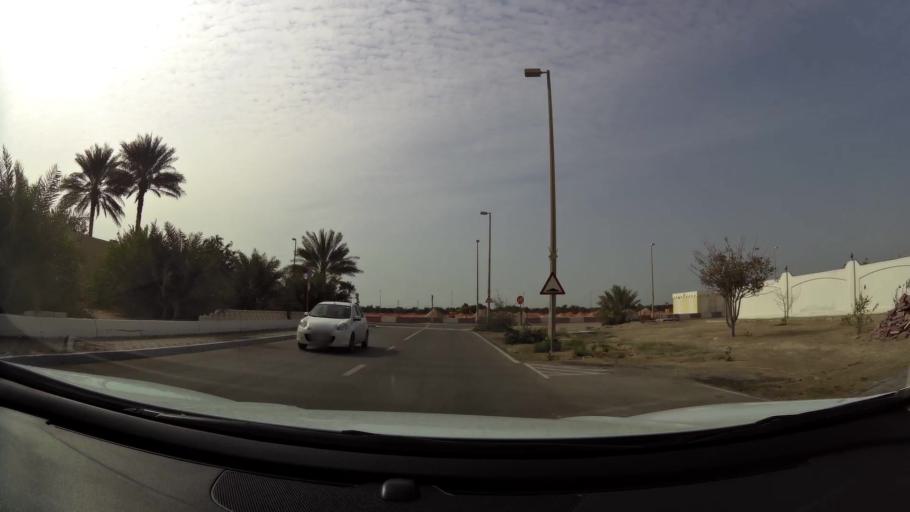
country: AE
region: Abu Dhabi
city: Abu Dhabi
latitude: 24.6018
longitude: 54.6979
